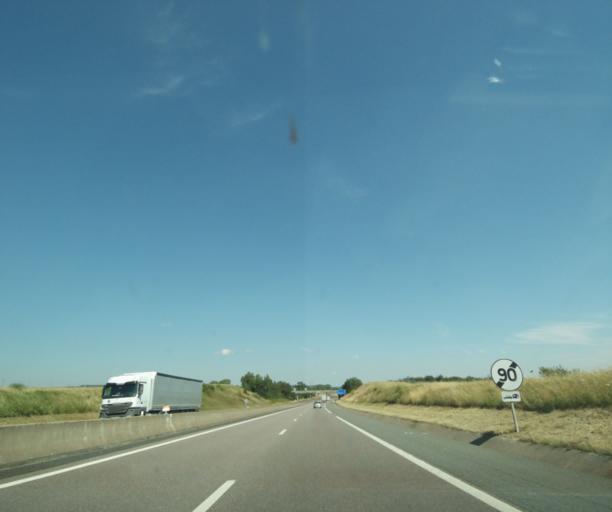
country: FR
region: Lorraine
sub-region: Departement de Meurthe-et-Moselle
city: Colombey-les-Belles
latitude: 48.5445
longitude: 5.8978
